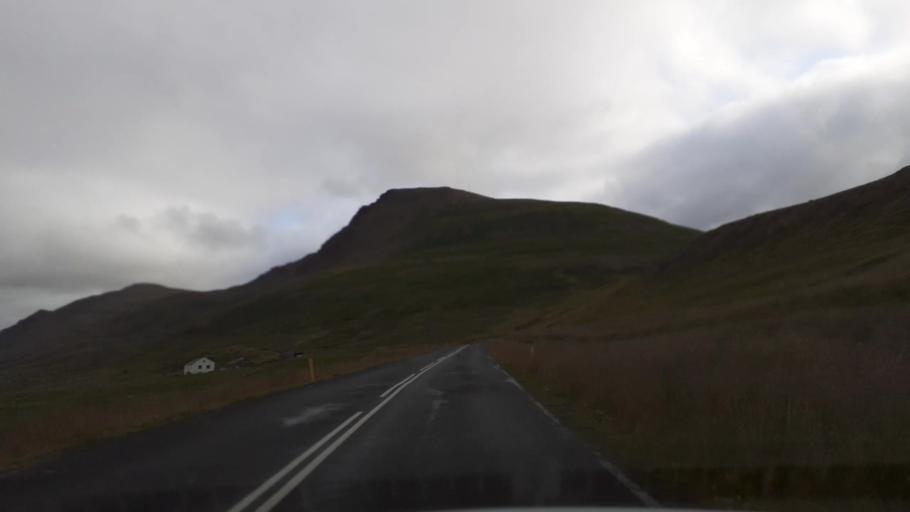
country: IS
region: Northeast
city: Akureyri
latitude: 65.8131
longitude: -18.0513
